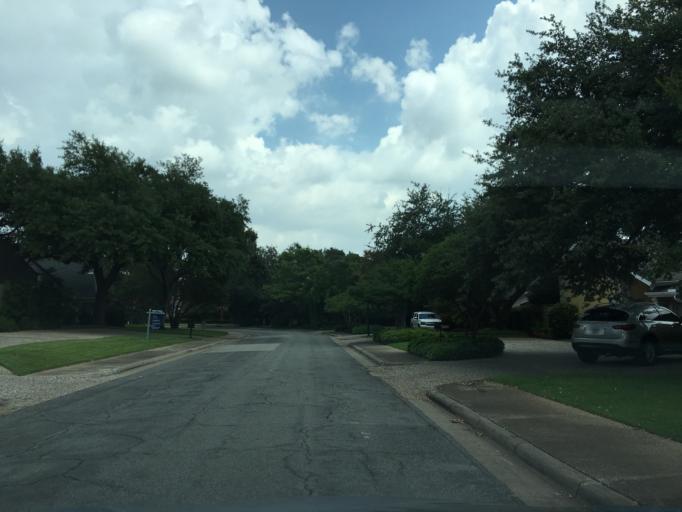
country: US
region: Texas
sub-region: Dallas County
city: University Park
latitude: 32.8900
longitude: -96.7857
